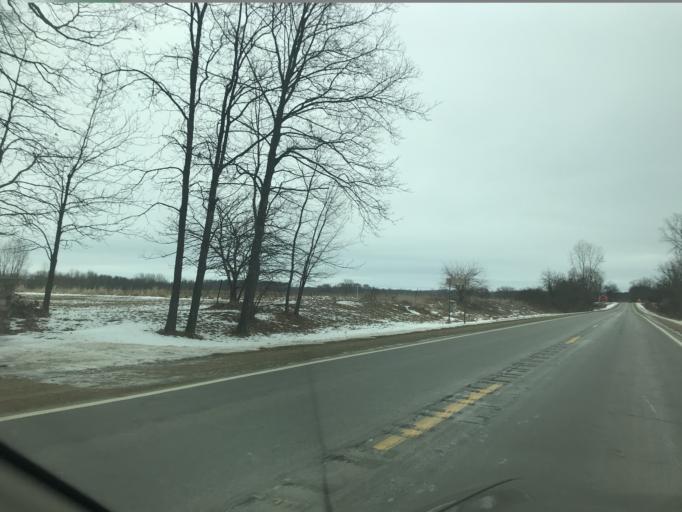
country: US
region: Michigan
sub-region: Eaton County
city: Eaton Rapids
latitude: 42.4148
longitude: -84.6202
